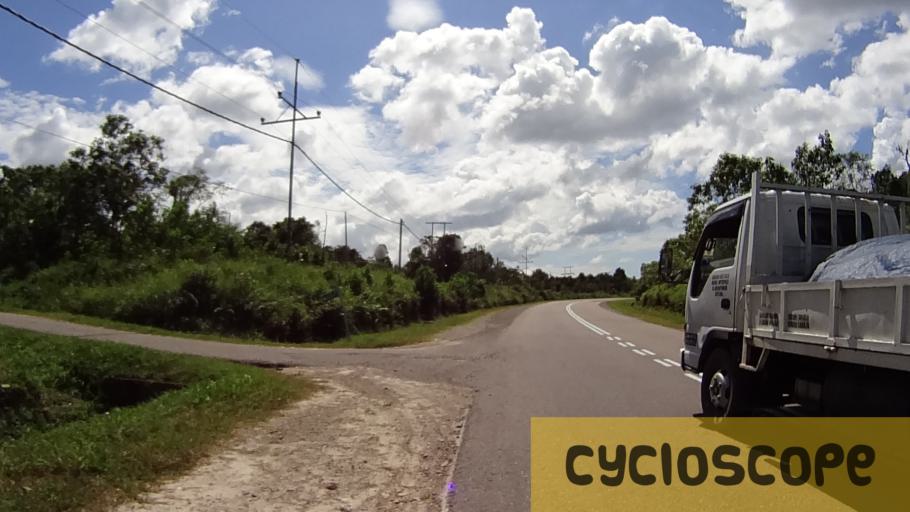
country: MY
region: Sabah
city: Beaufort
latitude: 5.1308
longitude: 115.6403
